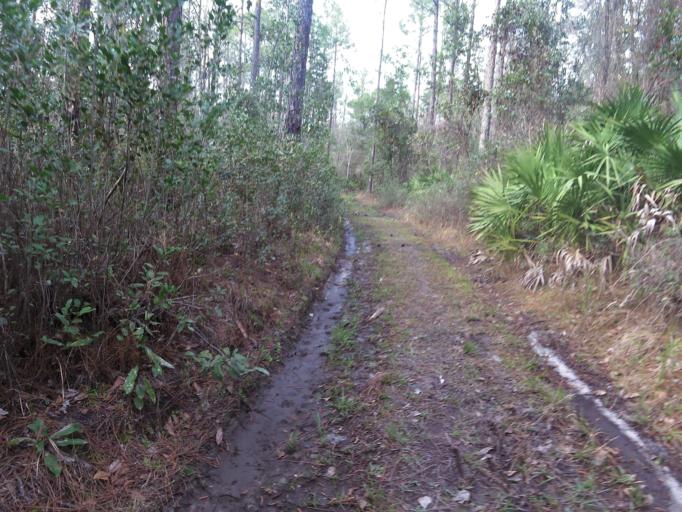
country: US
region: Florida
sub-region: Clay County
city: Middleburg
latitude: 30.1158
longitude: -81.8989
